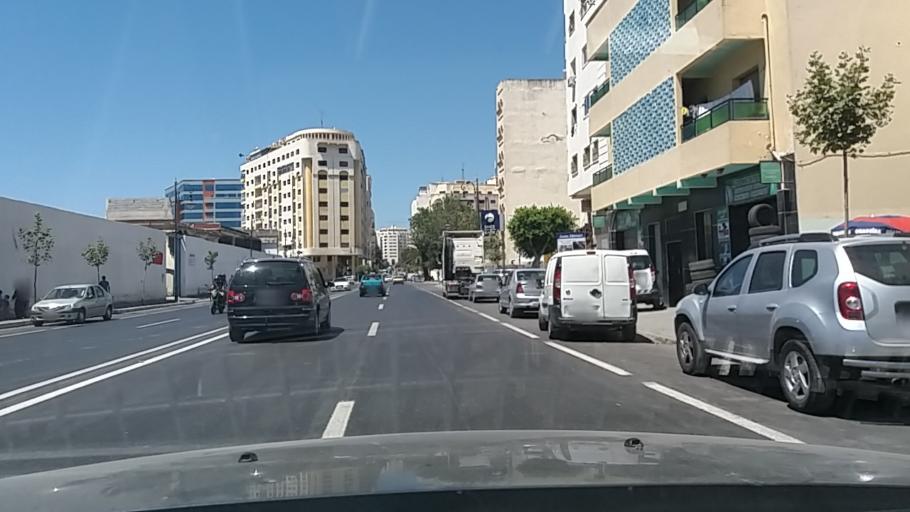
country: MA
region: Tanger-Tetouan
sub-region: Tanger-Assilah
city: Tangier
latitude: 35.7719
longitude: -5.7973
